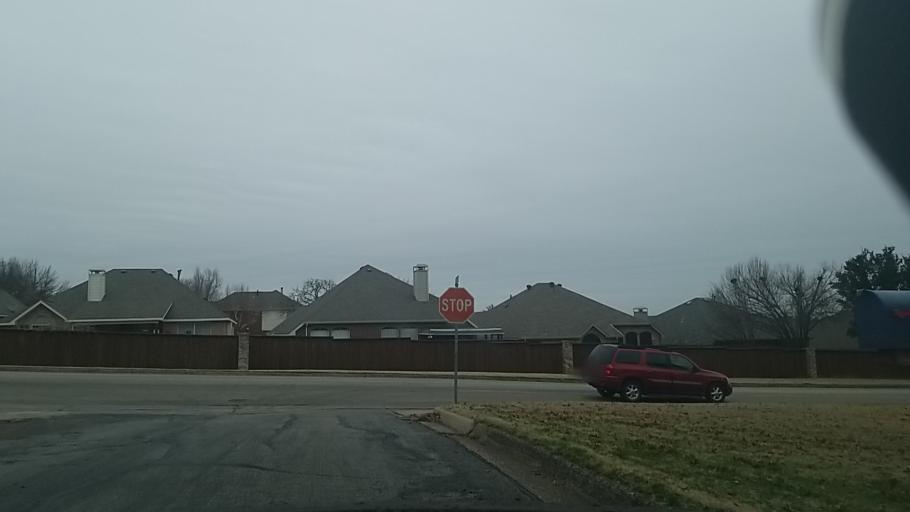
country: US
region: Texas
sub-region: Denton County
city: Corinth
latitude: 33.1552
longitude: -97.0738
